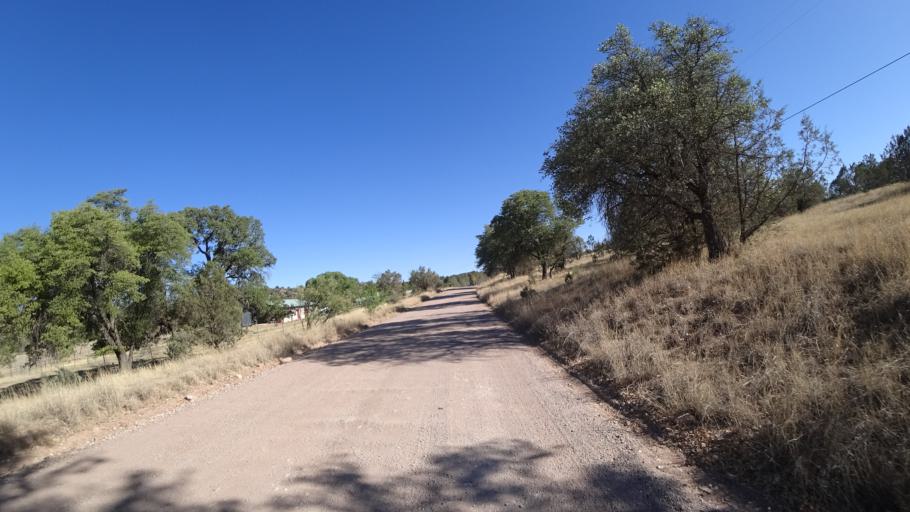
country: US
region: Arizona
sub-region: Cochise County
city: Huachuca City
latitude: 31.5358
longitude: -110.5293
